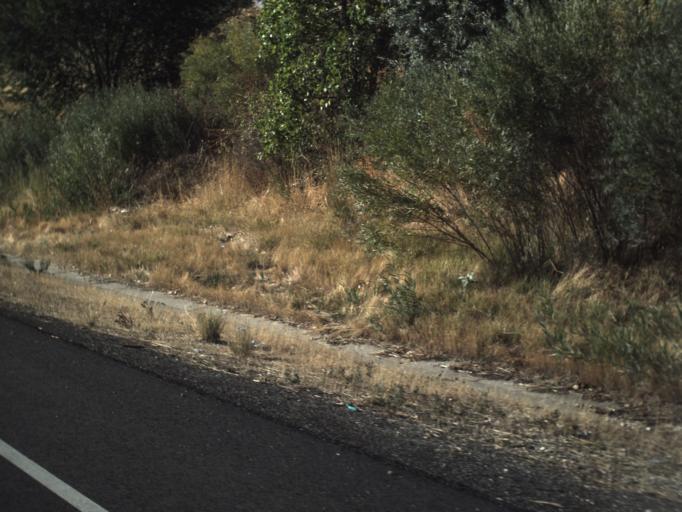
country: US
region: Utah
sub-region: Weber County
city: South Ogden
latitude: 41.2028
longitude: -111.9957
